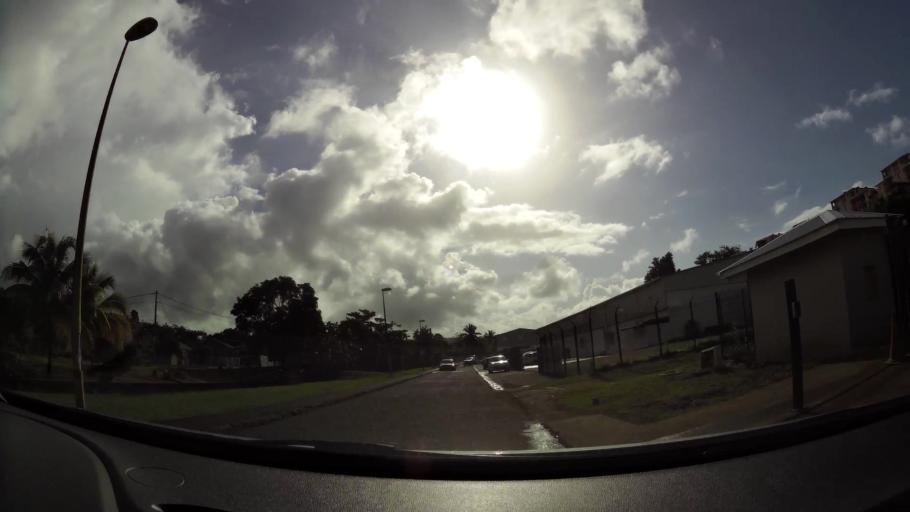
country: MQ
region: Martinique
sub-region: Martinique
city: Ducos
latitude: 14.5243
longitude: -60.9777
